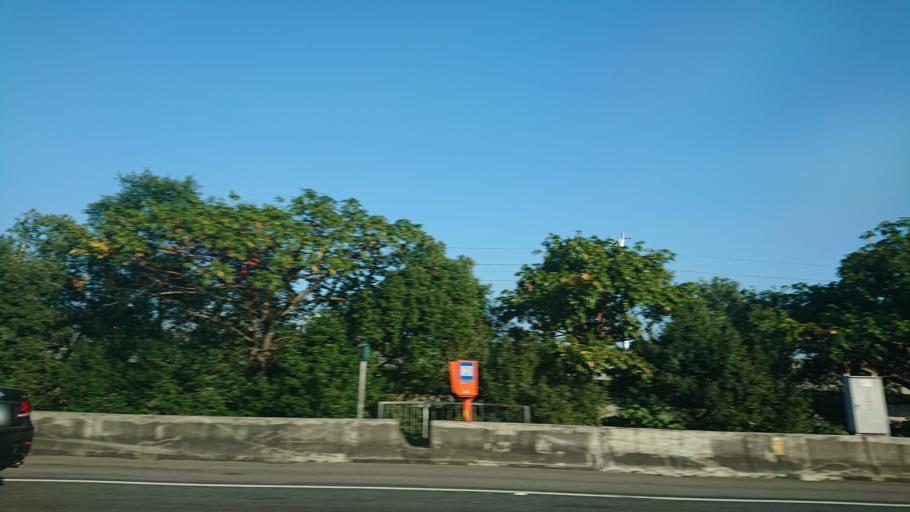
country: TW
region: Taiwan
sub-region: Taichung City
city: Taichung
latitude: 24.1388
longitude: 120.6180
